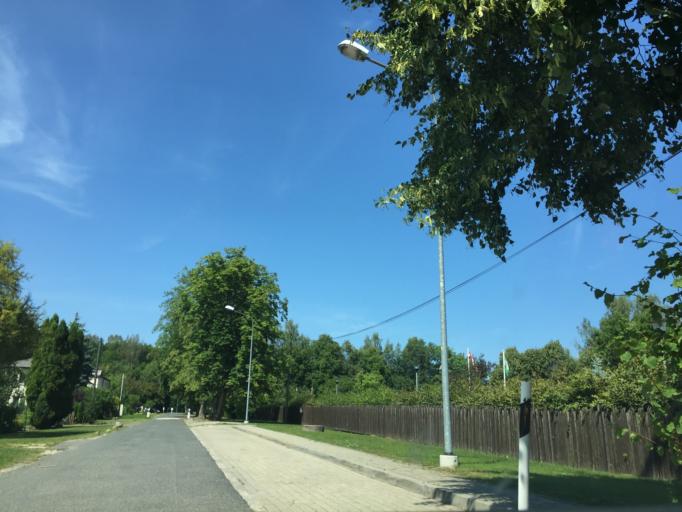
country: LV
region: Babite
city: Pinki
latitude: 56.9526
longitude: 23.9489
